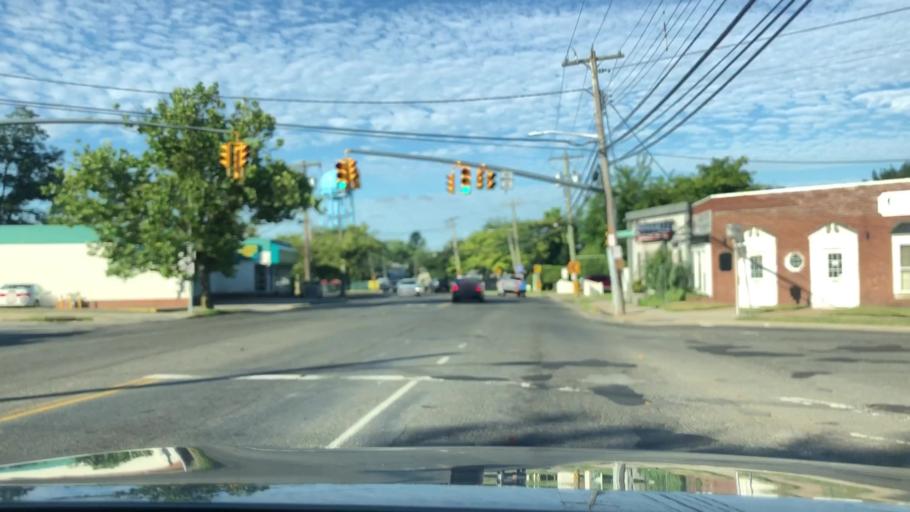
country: US
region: New York
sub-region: Nassau County
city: Franklin Square
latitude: 40.7014
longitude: -73.6808
